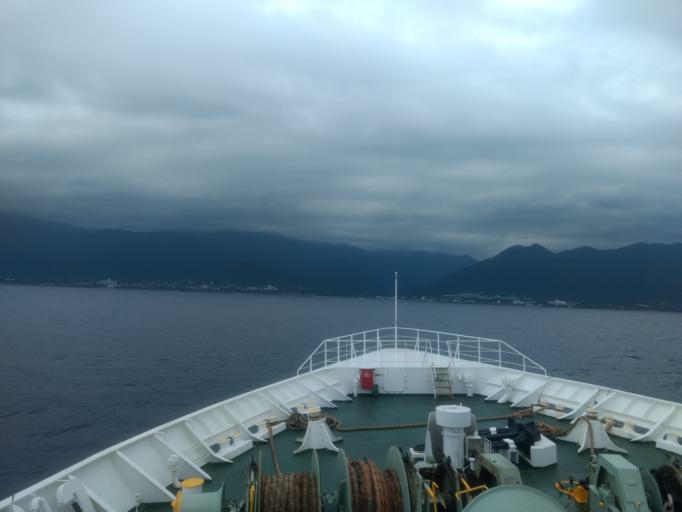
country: JP
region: Kagoshima
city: Nishinoomote
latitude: 30.4471
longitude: 130.5948
